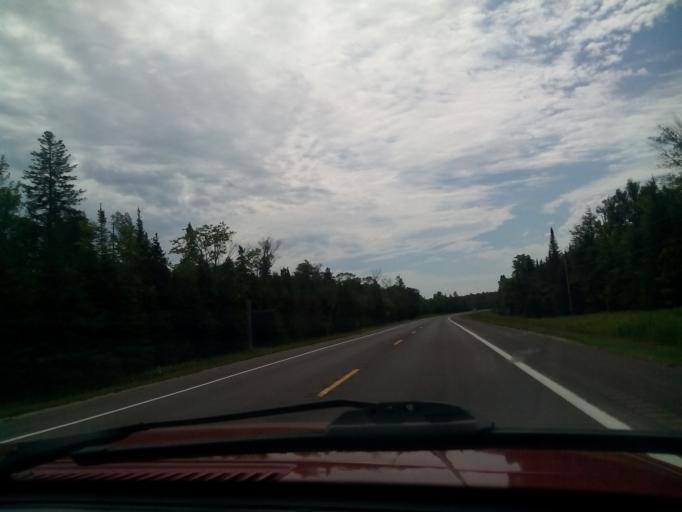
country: US
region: Michigan
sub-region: Schoolcraft County
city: Manistique
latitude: 46.0648
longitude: -85.9585
